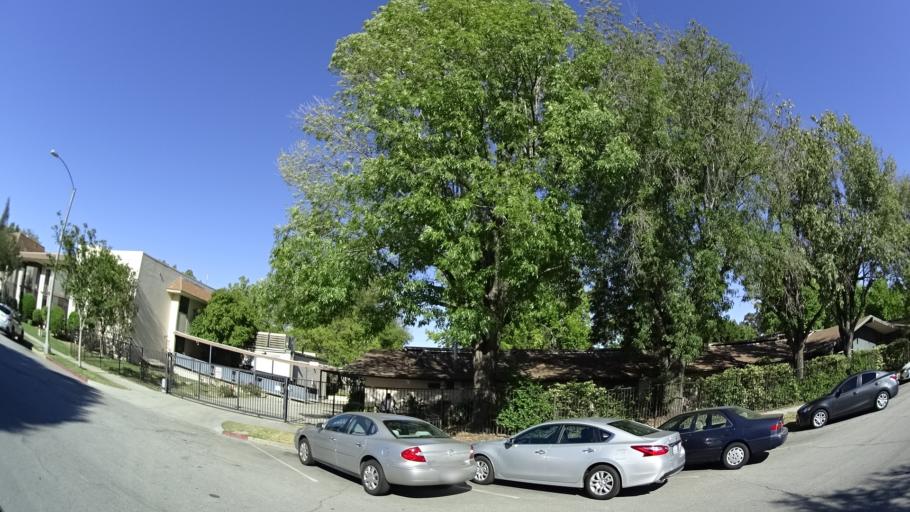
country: US
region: California
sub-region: Los Angeles County
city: Monterey Park
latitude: 34.0752
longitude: -118.1419
